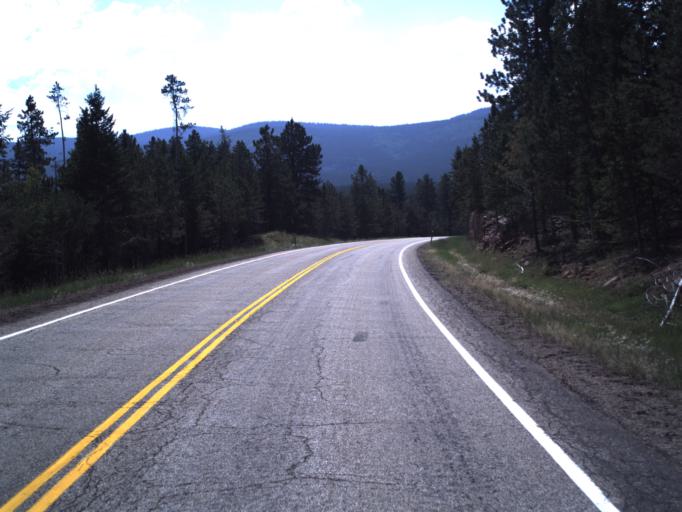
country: US
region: Utah
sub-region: Daggett County
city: Manila
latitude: 40.8465
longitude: -109.6663
